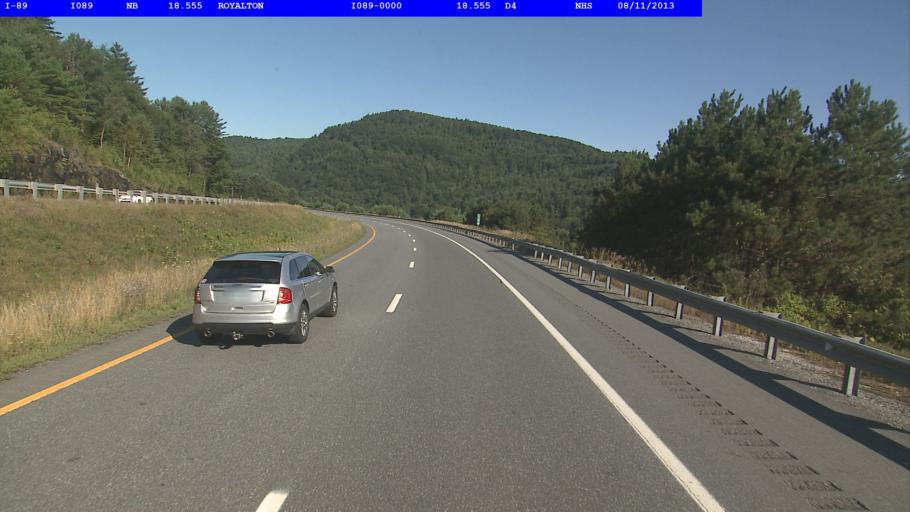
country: US
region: Vermont
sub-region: Orange County
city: Randolph
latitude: 43.8212
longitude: -72.5274
